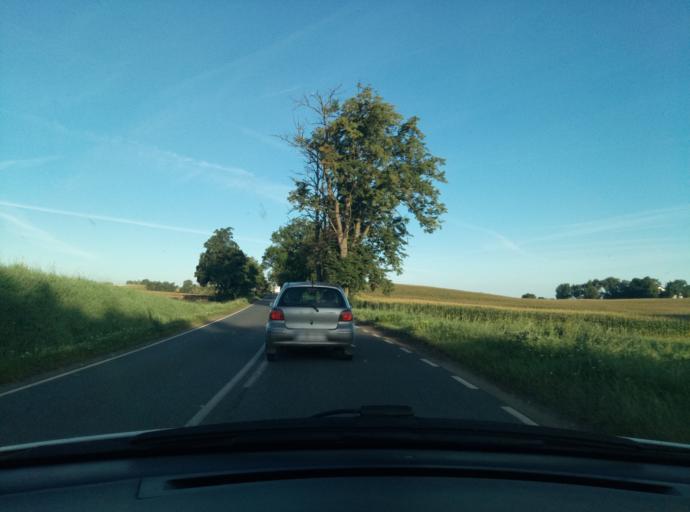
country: PL
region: Kujawsko-Pomorskie
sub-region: Powiat grudziadzki
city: Radzyn Chelminski
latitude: 53.3829
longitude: 18.9692
